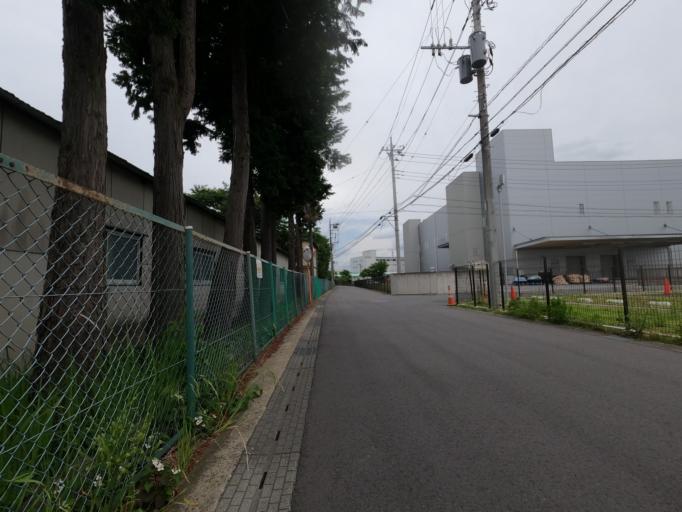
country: JP
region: Ibaraki
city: Moriya
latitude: 35.9606
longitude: 139.9816
